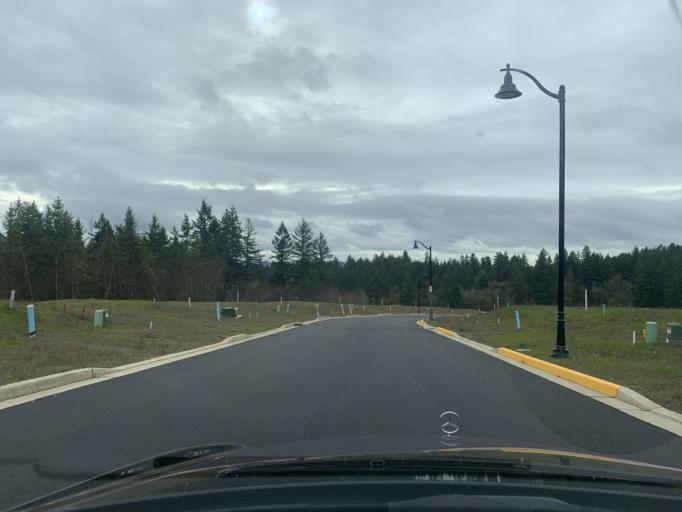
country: US
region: Oregon
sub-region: Clackamas County
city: Happy Valley
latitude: 45.4436
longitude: -122.5042
